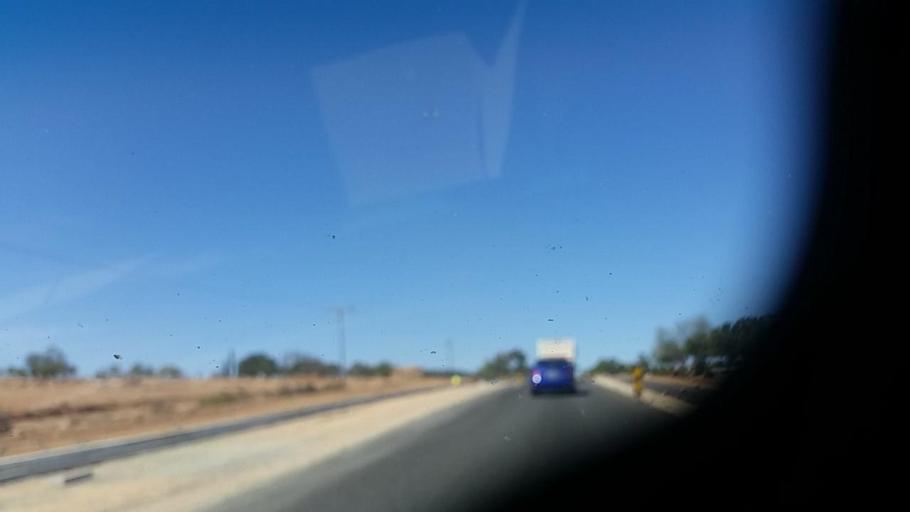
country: ZA
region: Western Cape
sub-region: Eden District Municipality
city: Oudtshoorn
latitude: -33.5934
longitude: 22.2282
